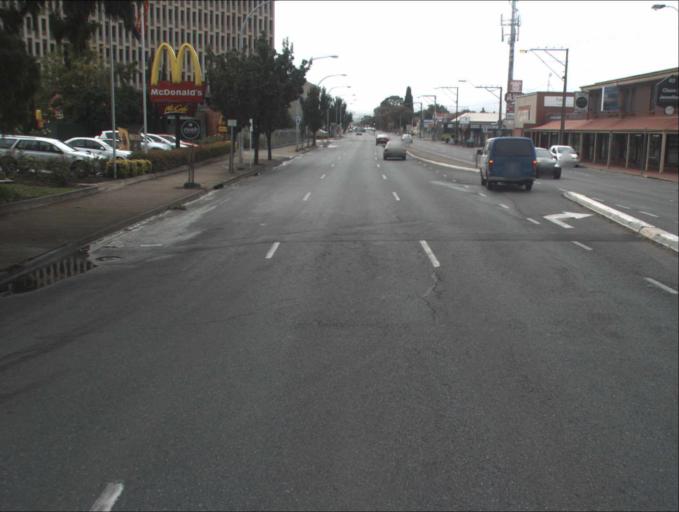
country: AU
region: South Australia
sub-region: Prospect
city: Prospect
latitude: -34.8894
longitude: 138.6131
